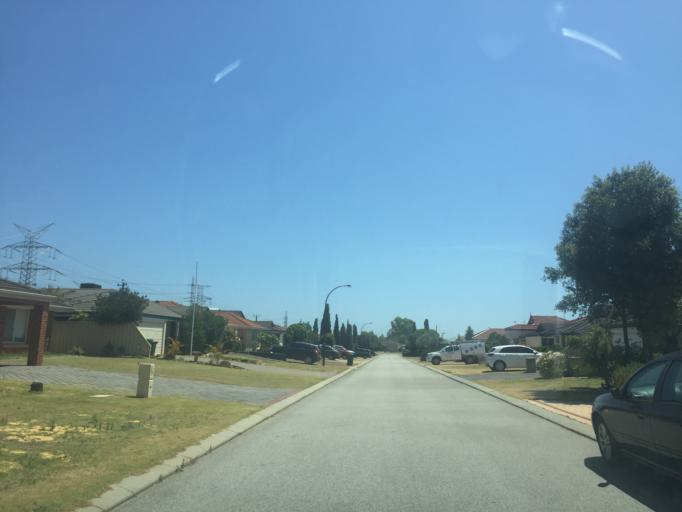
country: AU
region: Western Australia
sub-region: City of Cockburn
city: City of Cockburn
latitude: -32.0941
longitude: 115.8434
